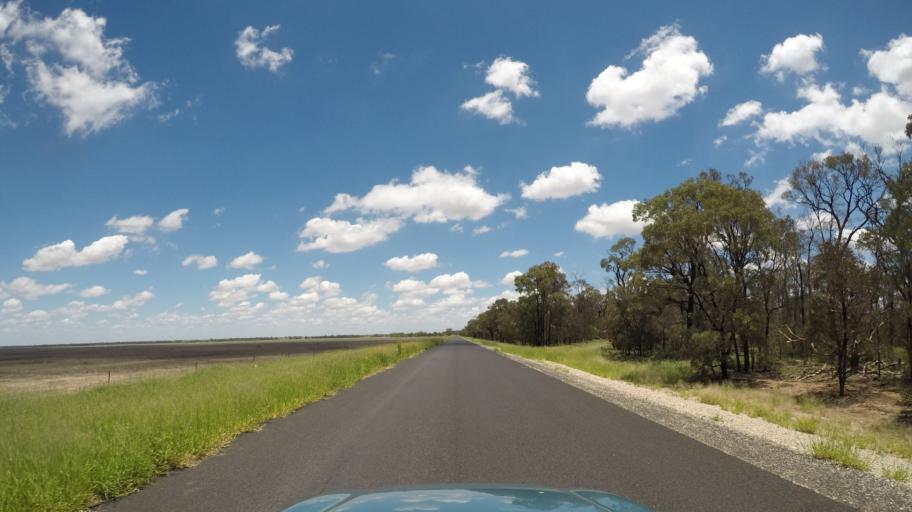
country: AU
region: Queensland
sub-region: Goondiwindi
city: Goondiwindi
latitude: -28.1583
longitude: 150.3907
